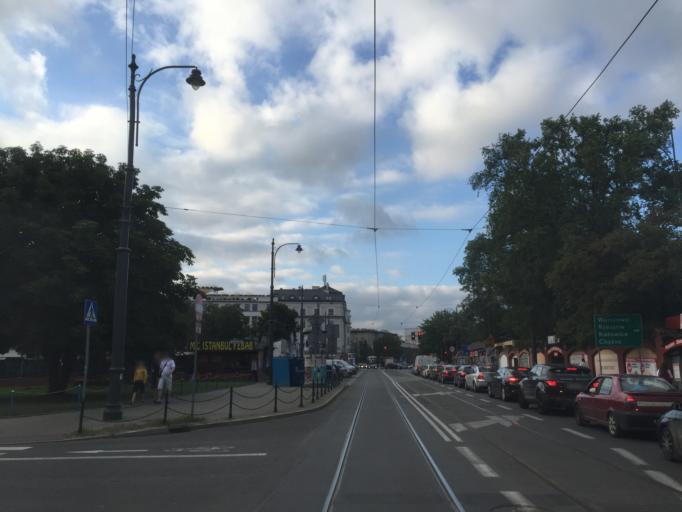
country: PL
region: Lesser Poland Voivodeship
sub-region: Krakow
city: Krakow
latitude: 50.0724
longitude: 19.9359
